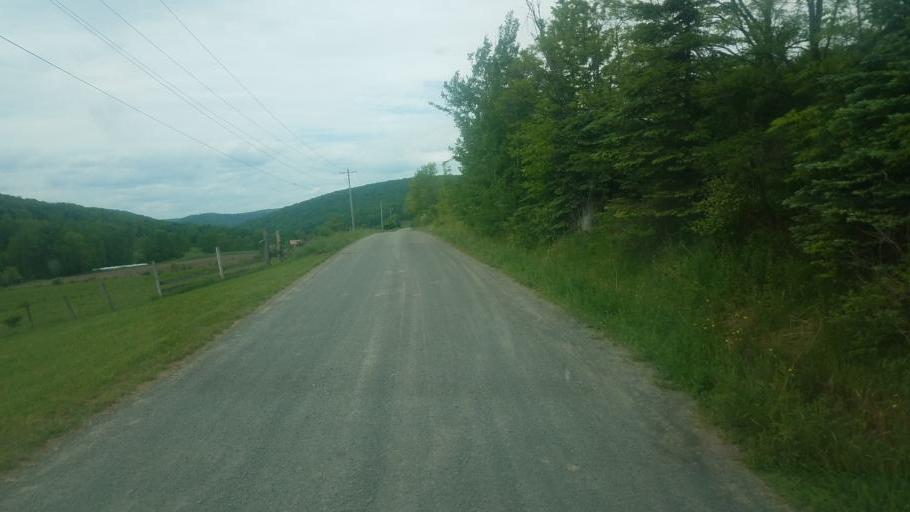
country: US
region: Pennsylvania
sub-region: Tioga County
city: Westfield
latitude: 41.8745
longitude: -77.5961
